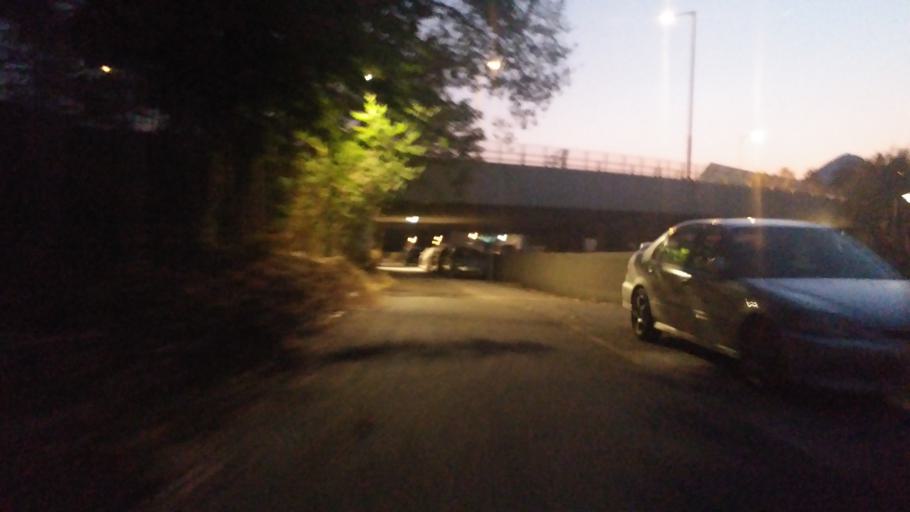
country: HK
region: Yuen Long
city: Yuen Long Kau Hui
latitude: 22.4470
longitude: 113.9978
